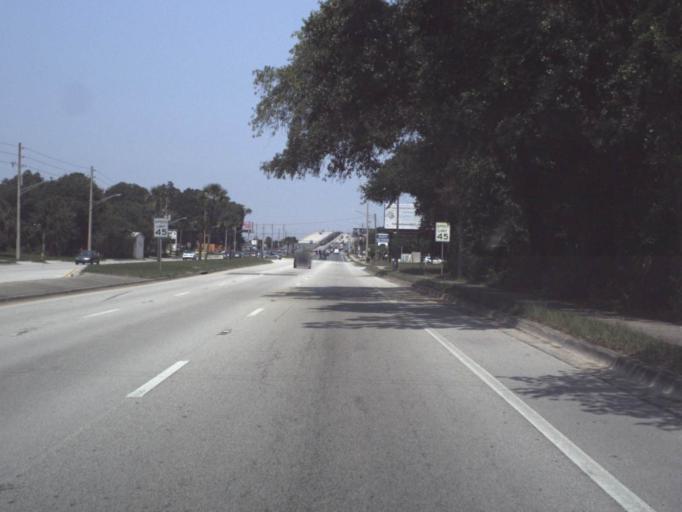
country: US
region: Florida
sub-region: Duval County
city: Atlantic Beach
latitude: 30.3210
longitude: -81.4492
